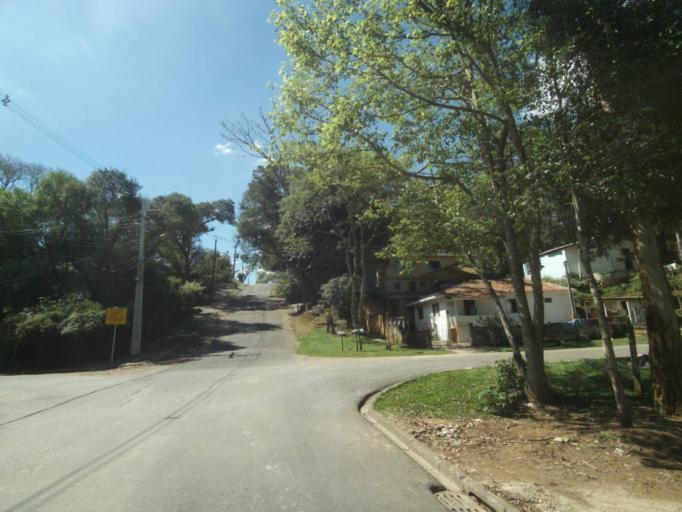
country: BR
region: Parana
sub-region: Curitiba
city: Curitiba
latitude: -25.3967
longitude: -49.2660
